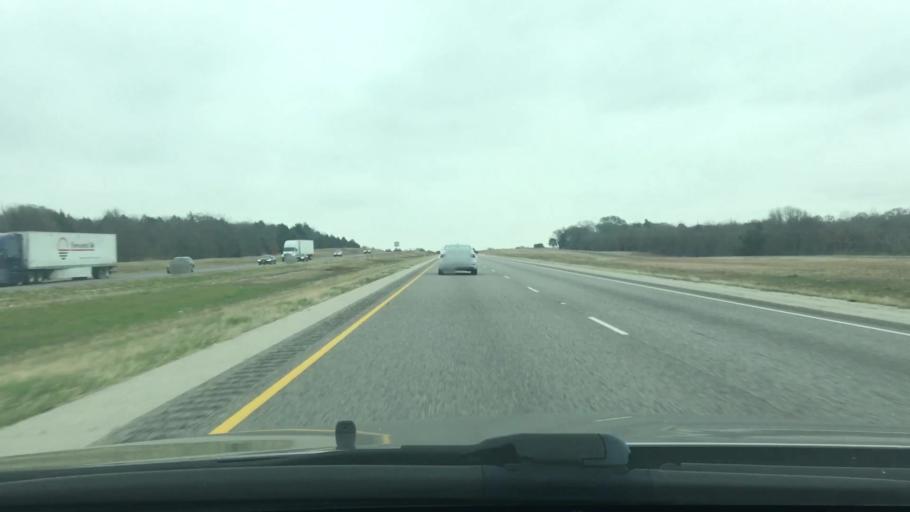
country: US
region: Texas
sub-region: Freestone County
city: Fairfield
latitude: 31.7880
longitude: -96.2440
